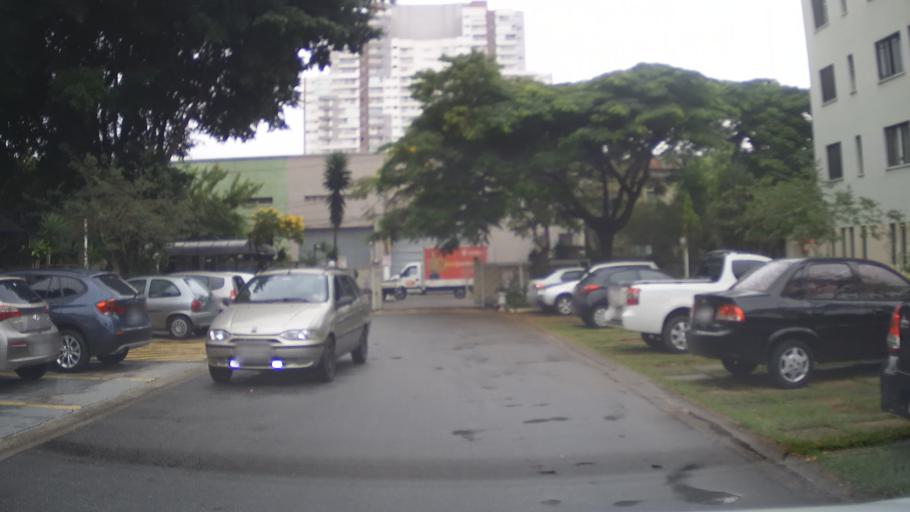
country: BR
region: Sao Paulo
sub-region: Sao Paulo
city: Sao Paulo
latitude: -23.5489
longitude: -46.6194
